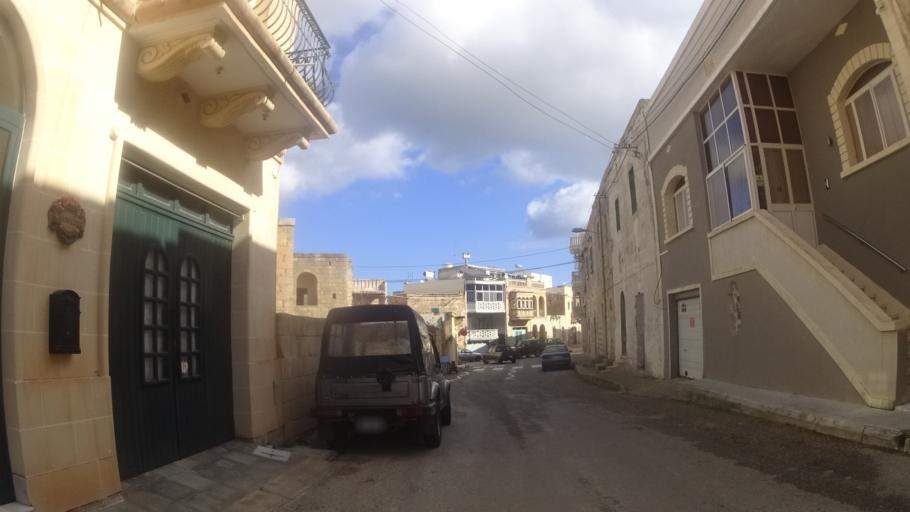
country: MT
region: In-Nadur
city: Nadur
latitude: 36.0388
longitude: 14.2886
